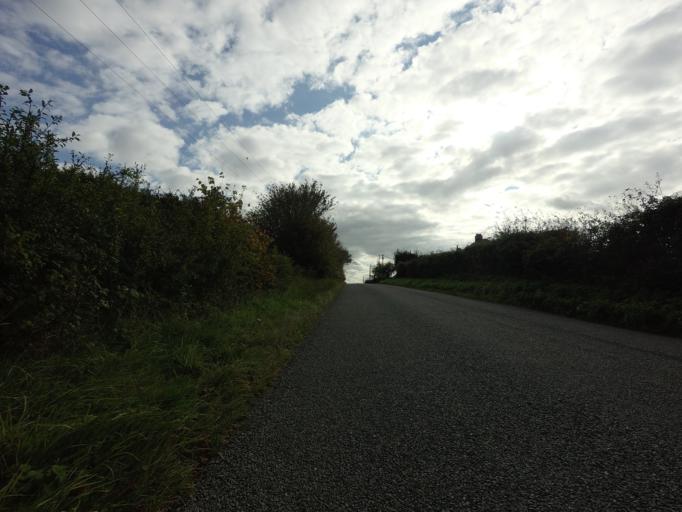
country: GB
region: England
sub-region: Norfolk
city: Snettisham
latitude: 52.9032
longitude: 0.5437
